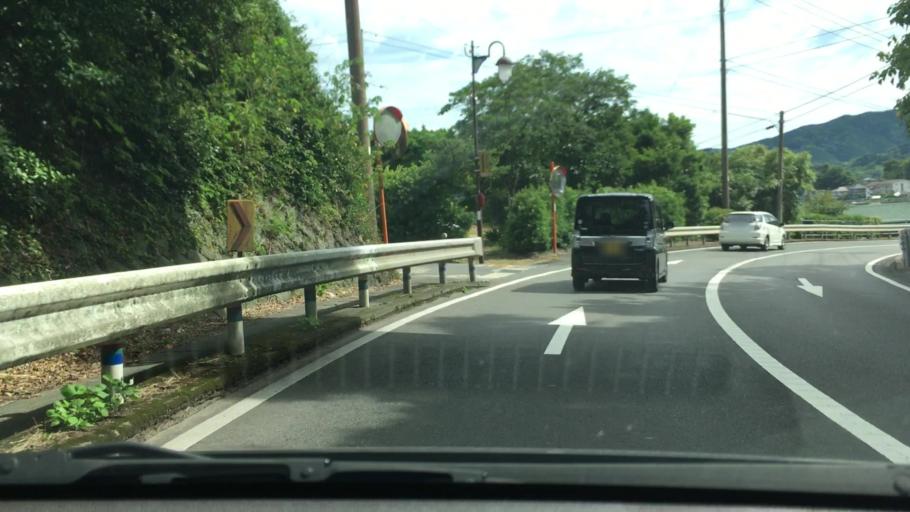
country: JP
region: Nagasaki
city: Togitsu
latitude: 32.9160
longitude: 129.7874
